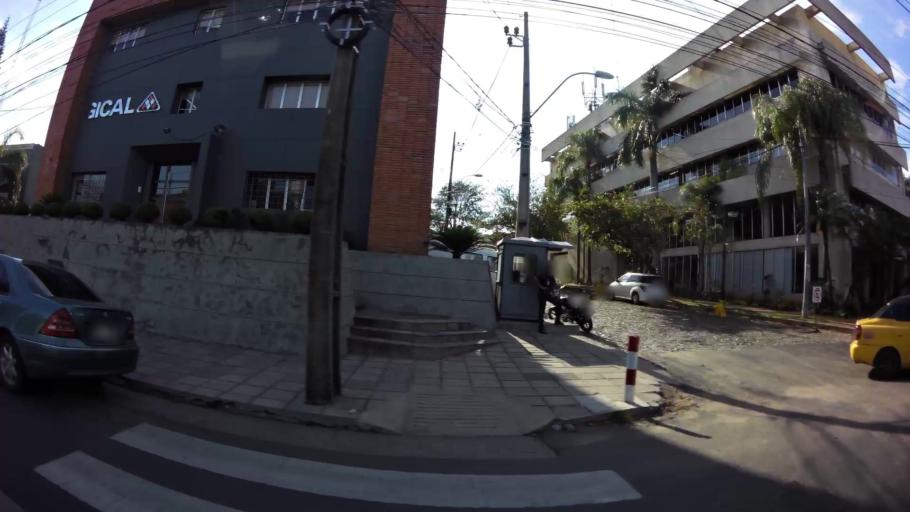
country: PY
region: Asuncion
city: Asuncion
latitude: -25.2807
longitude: -57.6158
